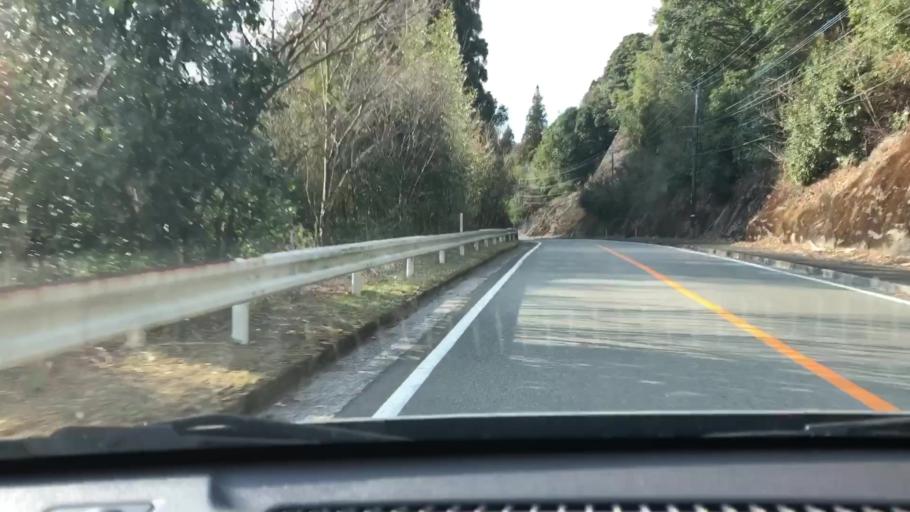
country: JP
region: Miyazaki
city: Miyazaki-shi
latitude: 31.8190
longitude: 131.2995
